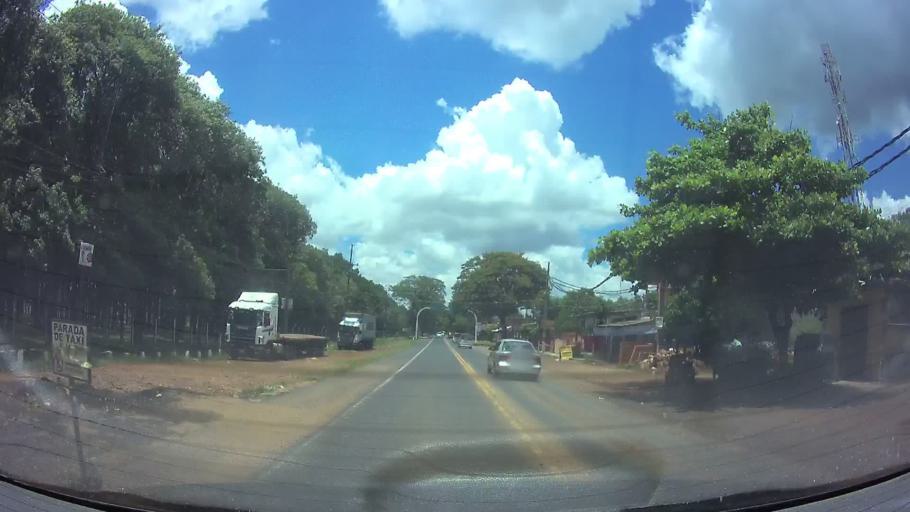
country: PY
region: Central
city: Capiata
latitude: -25.3616
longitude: -57.4278
